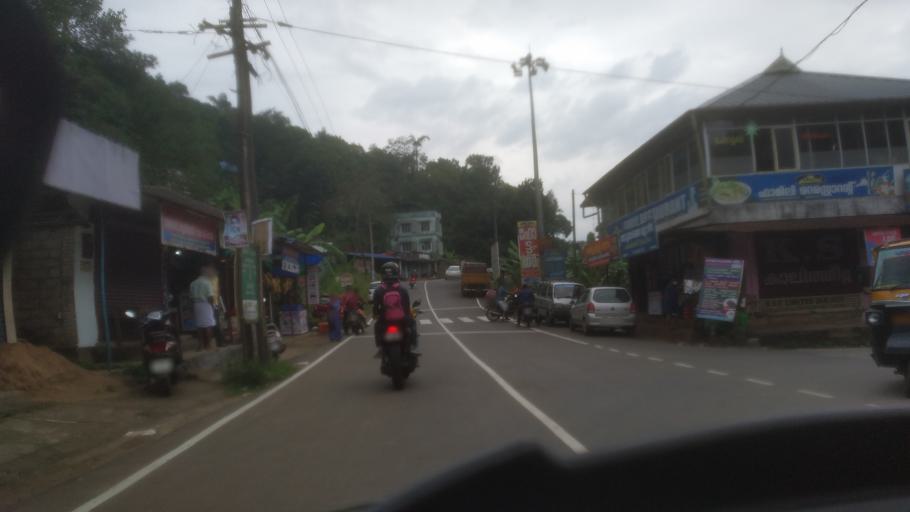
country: IN
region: Kerala
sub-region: Idukki
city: Idukki
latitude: 9.9459
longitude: 77.0151
